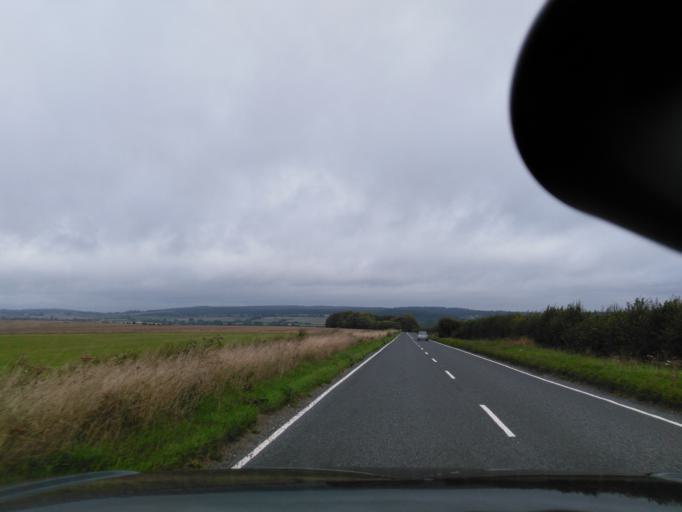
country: GB
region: England
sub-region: Wiltshire
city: Bishopstrow
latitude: 51.1498
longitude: -2.1647
